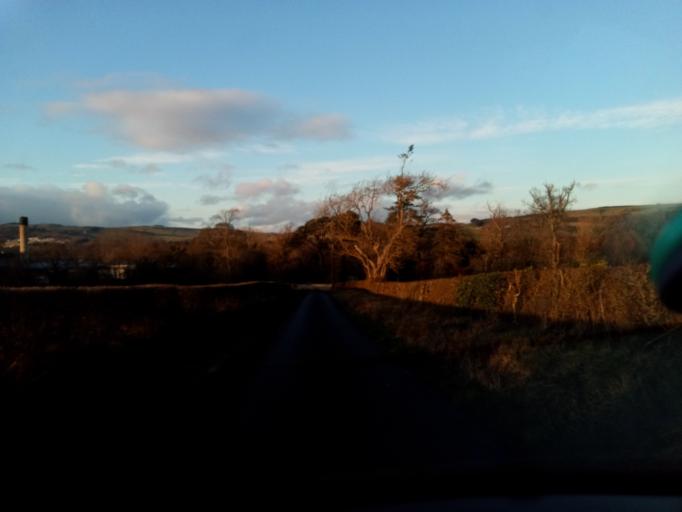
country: GB
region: Scotland
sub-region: The Scottish Borders
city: Melrose
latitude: 55.5939
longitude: -2.7374
